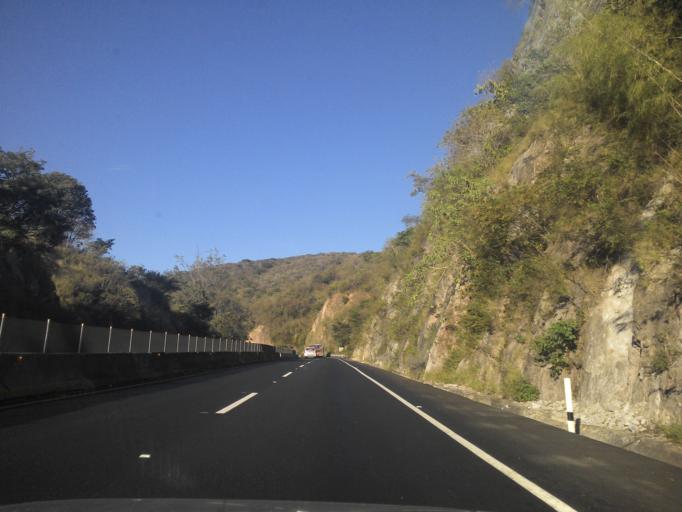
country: MX
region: Jalisco
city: Hostotipaquillo
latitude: 21.0033
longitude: -104.2031
